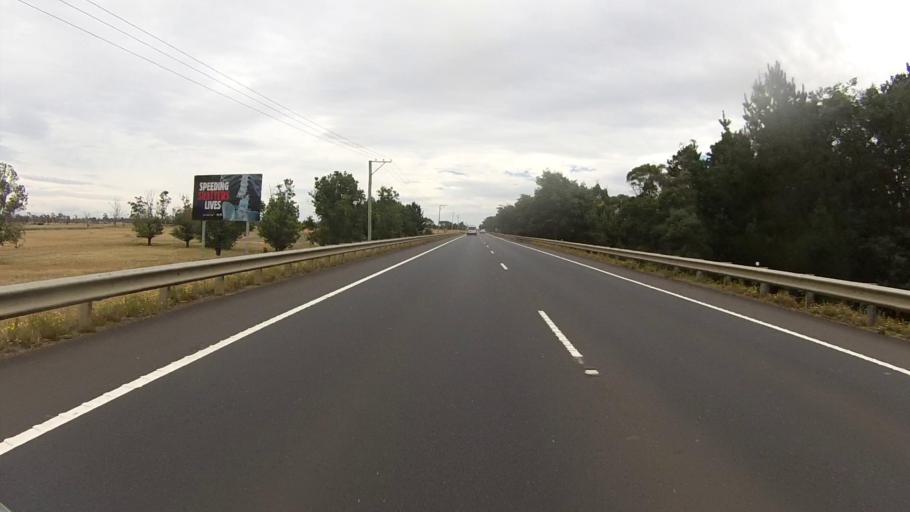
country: AU
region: Tasmania
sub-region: Northern Midlands
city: Evandale
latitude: -41.6921
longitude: 147.2833
